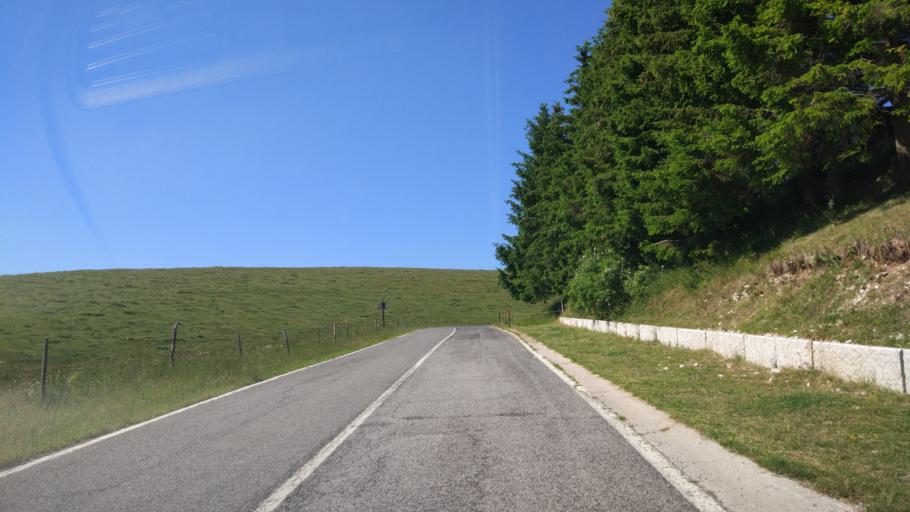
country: IT
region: Veneto
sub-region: Provincia di Verona
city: Erbezzo
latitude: 45.6809
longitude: 10.9808
